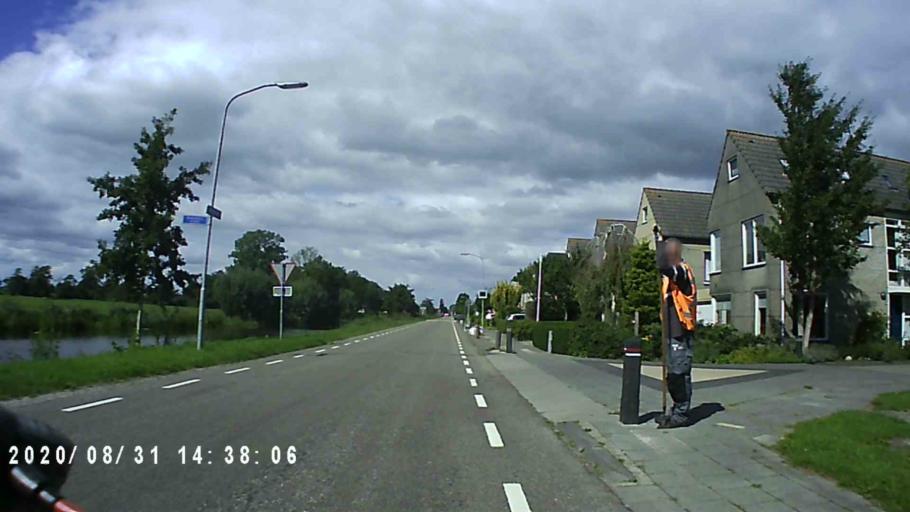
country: NL
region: Groningen
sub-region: Gemeente Zuidhorn
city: Zuidhorn
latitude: 53.2392
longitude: 6.3917
